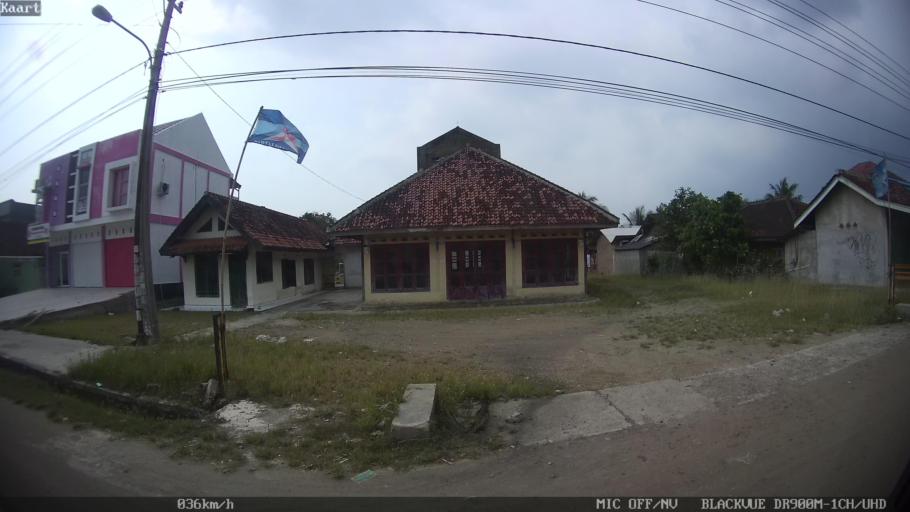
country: ID
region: Lampung
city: Gadingrejo
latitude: -5.3772
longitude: 105.0348
